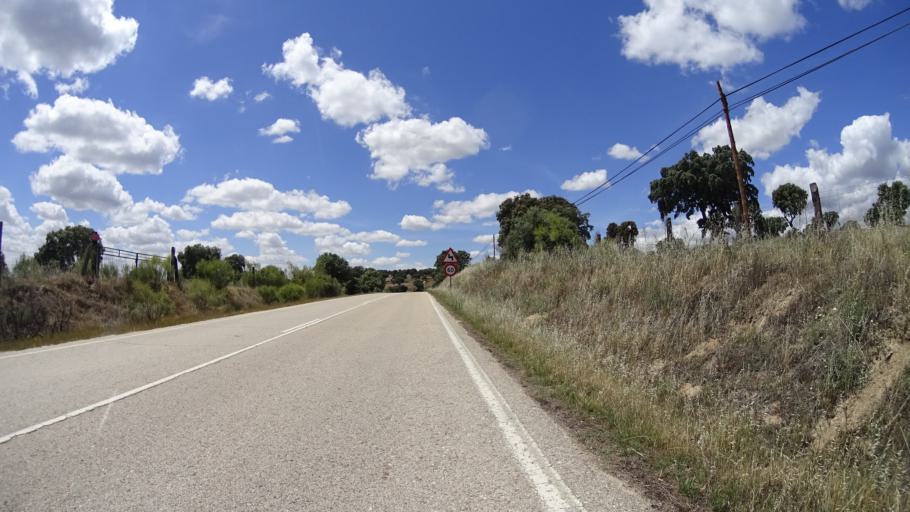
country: ES
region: Madrid
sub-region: Provincia de Madrid
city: Villanueva del Pardillo
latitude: 40.4535
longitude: -3.9523
